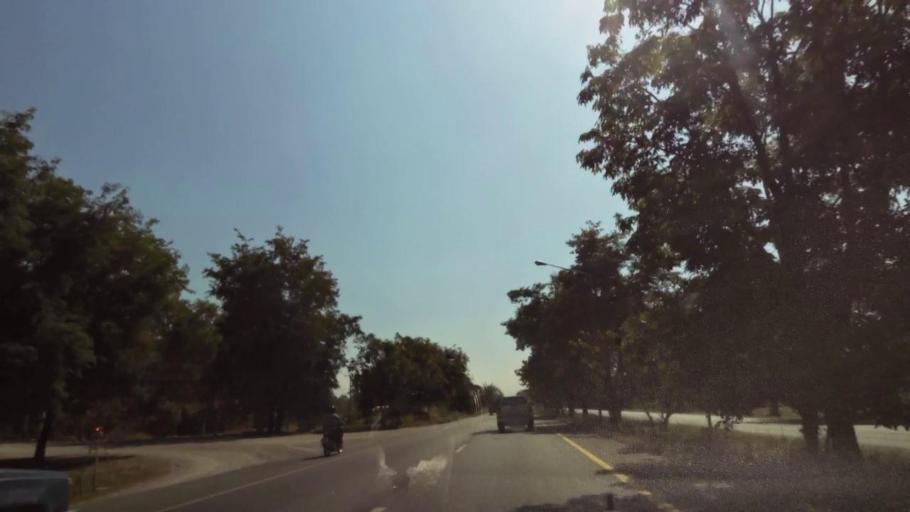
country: TH
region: Nakhon Sawan
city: Kao Liao
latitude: 15.8512
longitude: 100.1172
